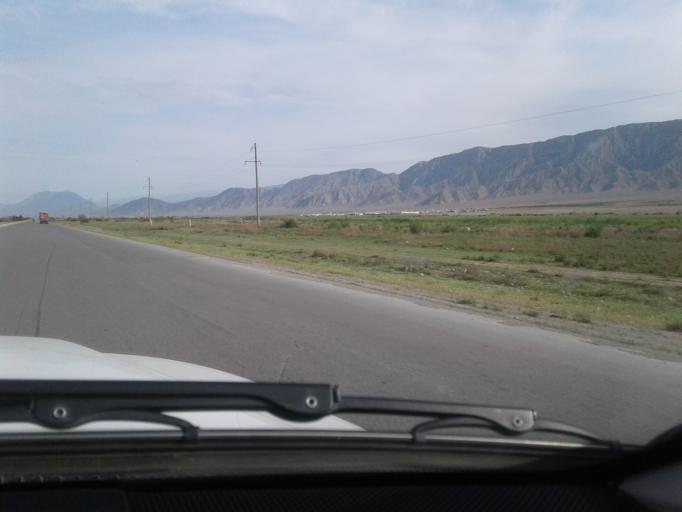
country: TM
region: Ahal
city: Arcabil
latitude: 38.2047
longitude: 57.8206
